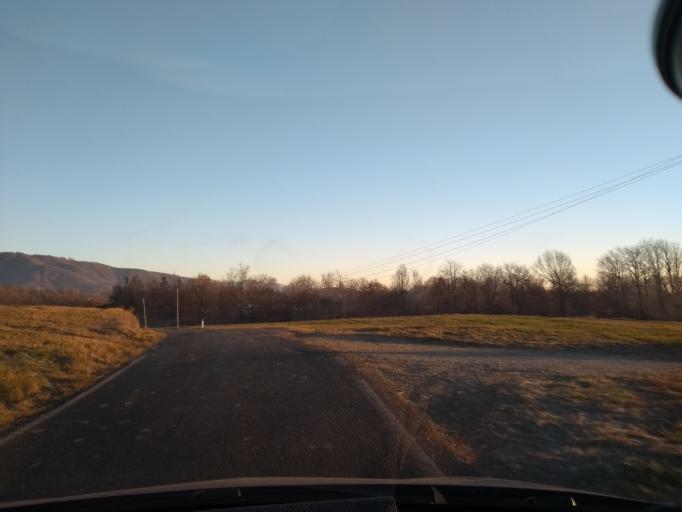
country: IT
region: Piedmont
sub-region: Provincia di Torino
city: Mathi
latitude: 45.2800
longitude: 7.5428
